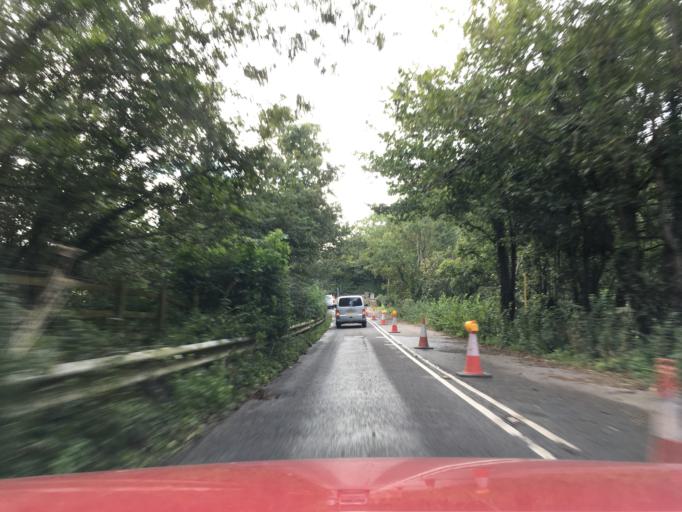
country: GB
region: England
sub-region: Devon
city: Modbury
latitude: 50.3504
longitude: -3.9080
